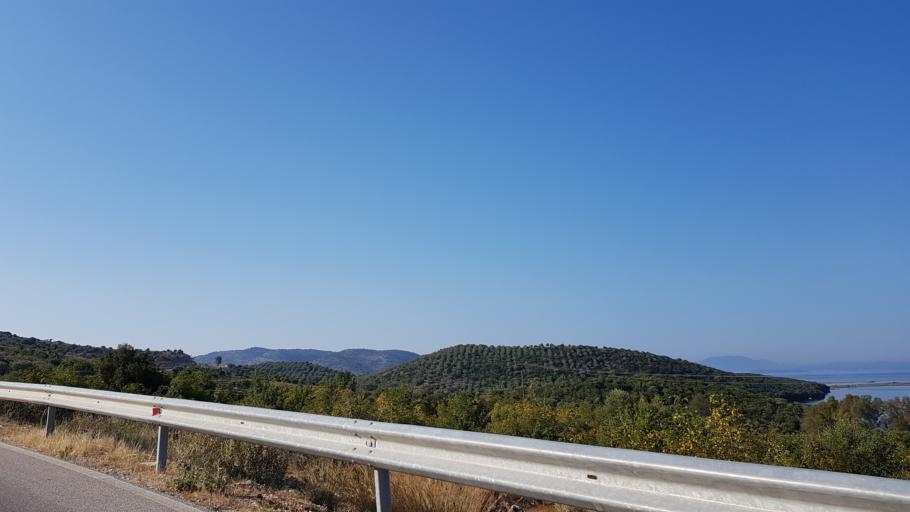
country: AL
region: Vlore
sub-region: Rrethi i Sarandes
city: Xarre
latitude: 39.7558
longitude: 20.0021
